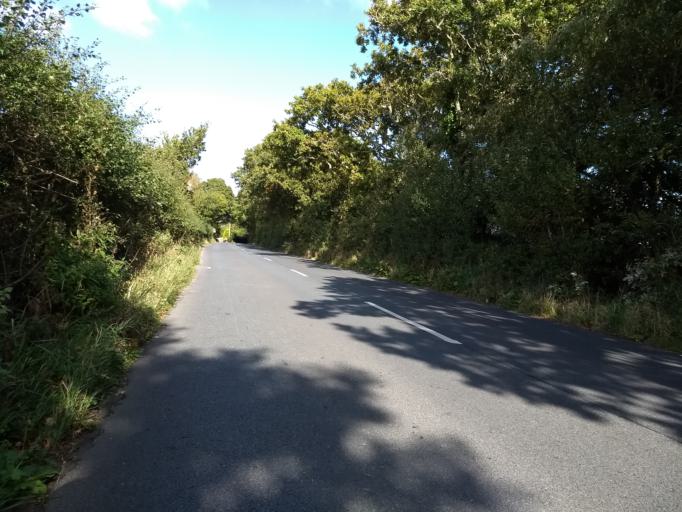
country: GB
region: England
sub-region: Isle of Wight
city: Seaview
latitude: 50.7042
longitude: -1.1150
